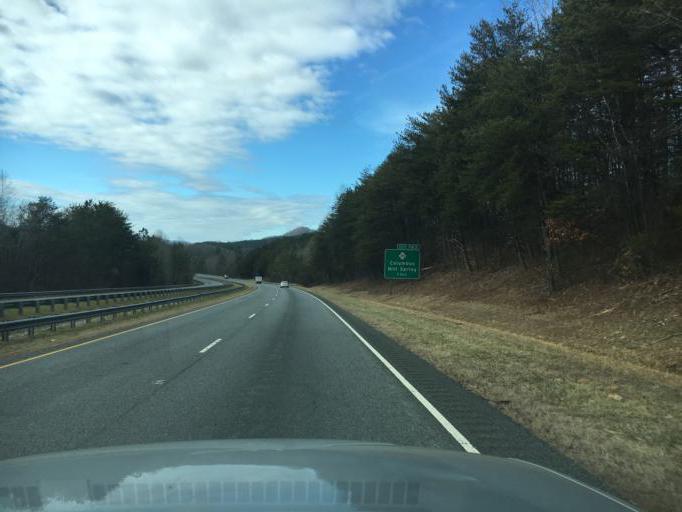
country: US
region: North Carolina
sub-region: Polk County
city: Columbus
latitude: 35.2696
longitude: -82.1639
